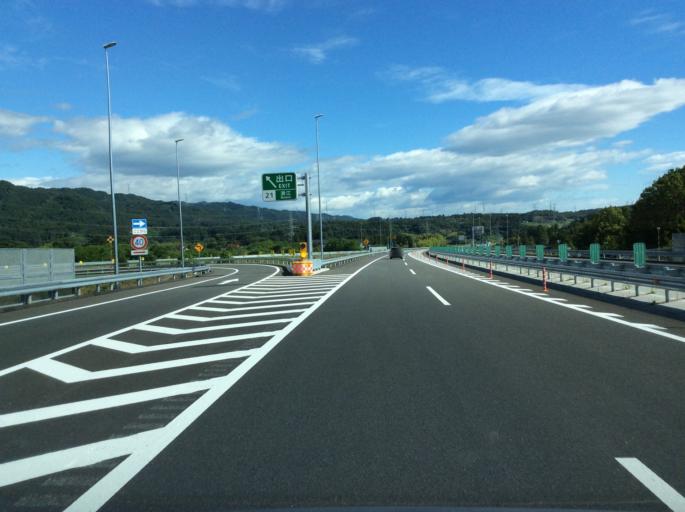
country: JP
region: Fukushima
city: Namie
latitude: 37.4985
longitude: 140.9430
